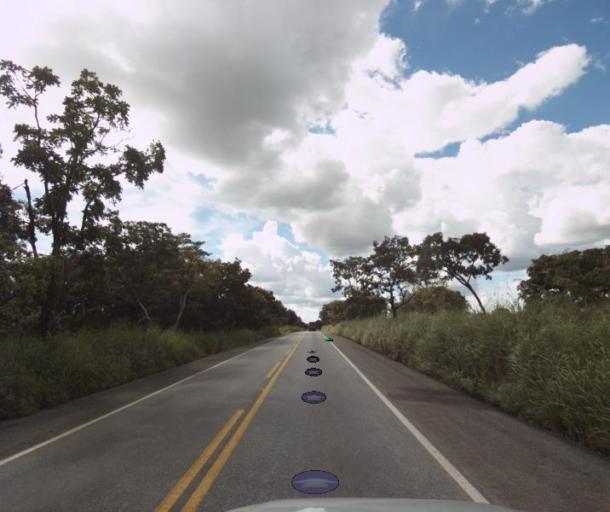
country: BR
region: Goias
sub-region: Porangatu
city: Porangatu
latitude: -13.2930
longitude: -49.1239
